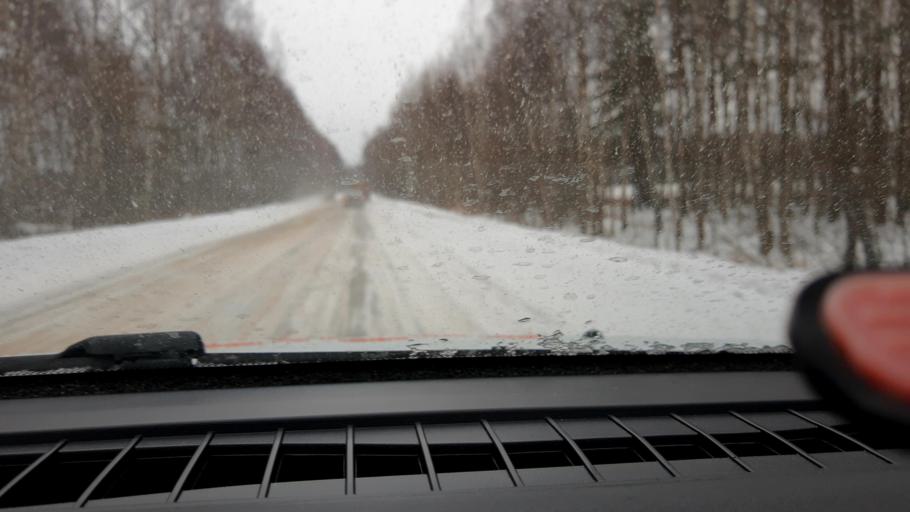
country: RU
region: Nizjnij Novgorod
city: Pamyat' Parizhskoy Kommuny
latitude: 56.2577
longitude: 44.4596
